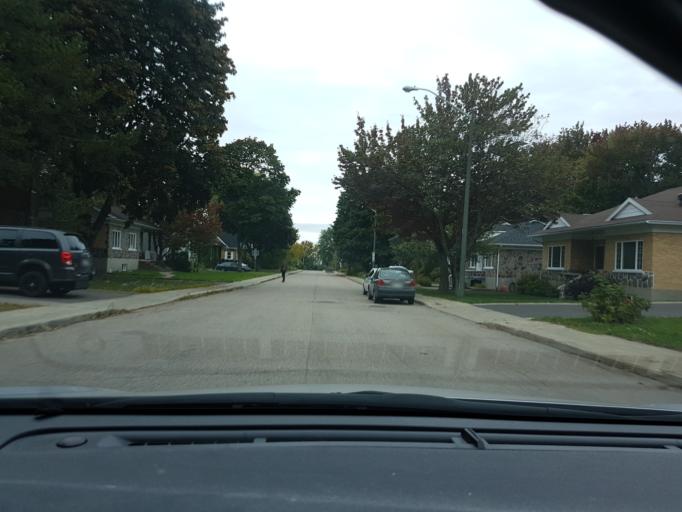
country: CA
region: Quebec
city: Quebec
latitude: 46.7877
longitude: -71.2640
